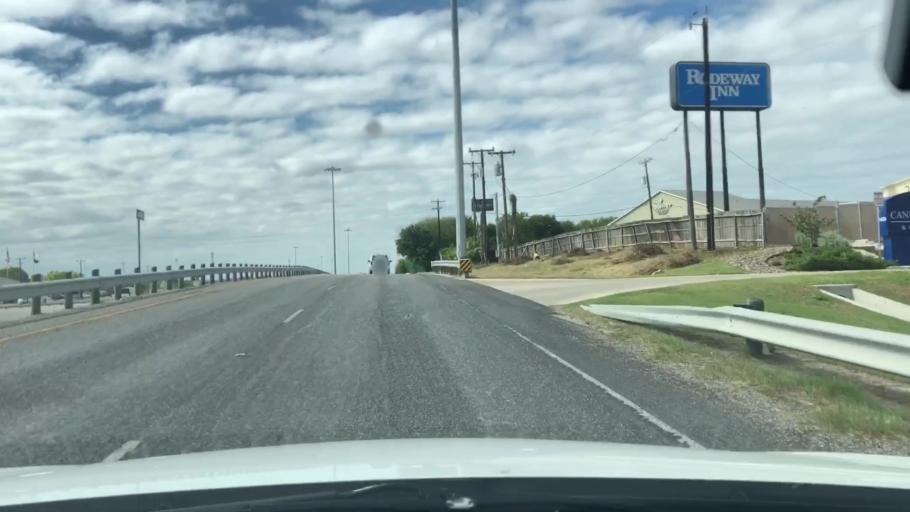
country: US
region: Texas
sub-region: Bexar County
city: Lackland Air Force Base
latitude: 29.4052
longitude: -98.6157
